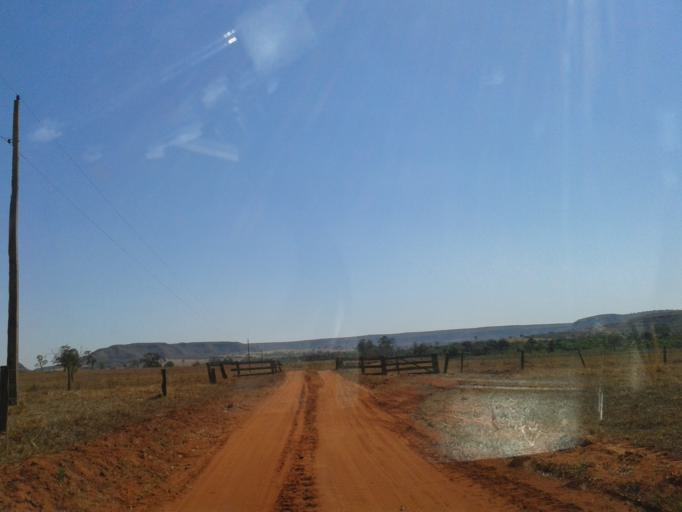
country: BR
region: Minas Gerais
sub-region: Santa Vitoria
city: Santa Vitoria
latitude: -19.0718
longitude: -50.0415
